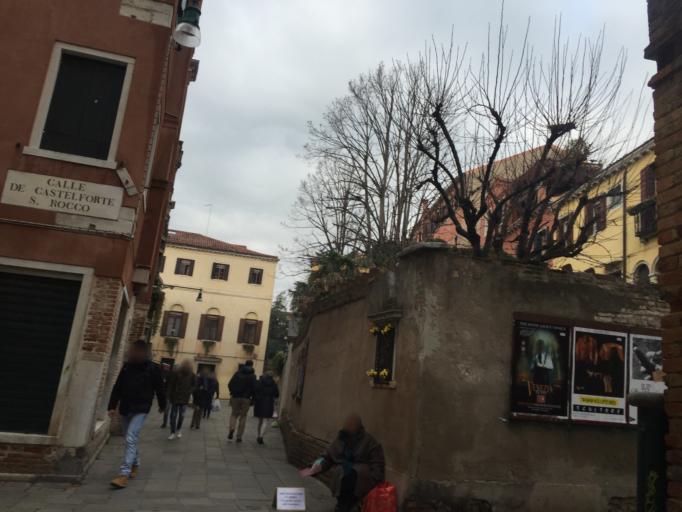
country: IT
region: Veneto
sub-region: Provincia di Venezia
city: Venice
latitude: 45.4370
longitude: 12.3248
